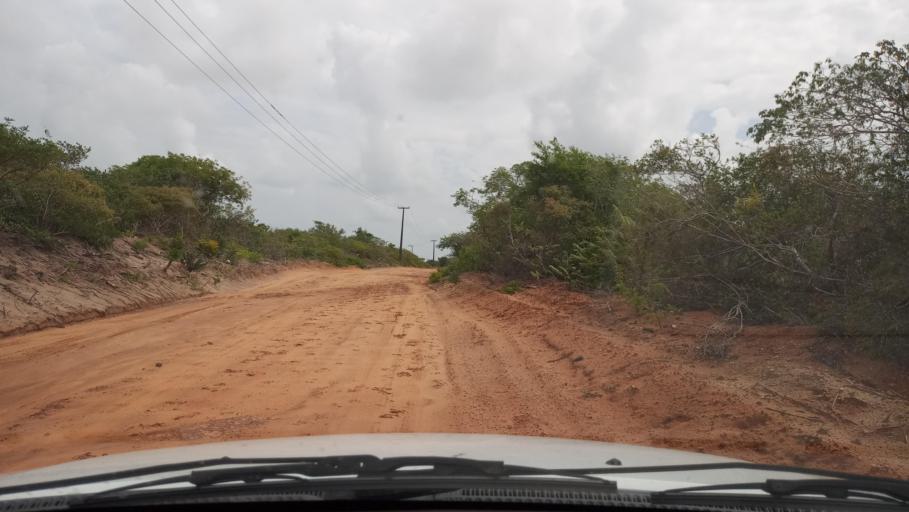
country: BR
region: Rio Grande do Norte
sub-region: Maxaranguape
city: Sao Miguel
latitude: -5.4715
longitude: -35.3004
